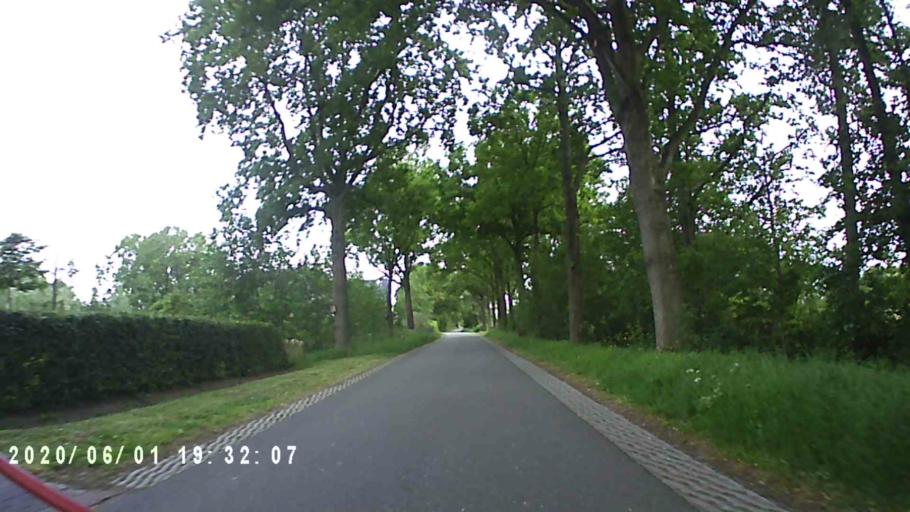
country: NL
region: Friesland
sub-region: Gemeente Achtkarspelen
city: Augustinusga
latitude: 53.2127
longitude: 6.1574
